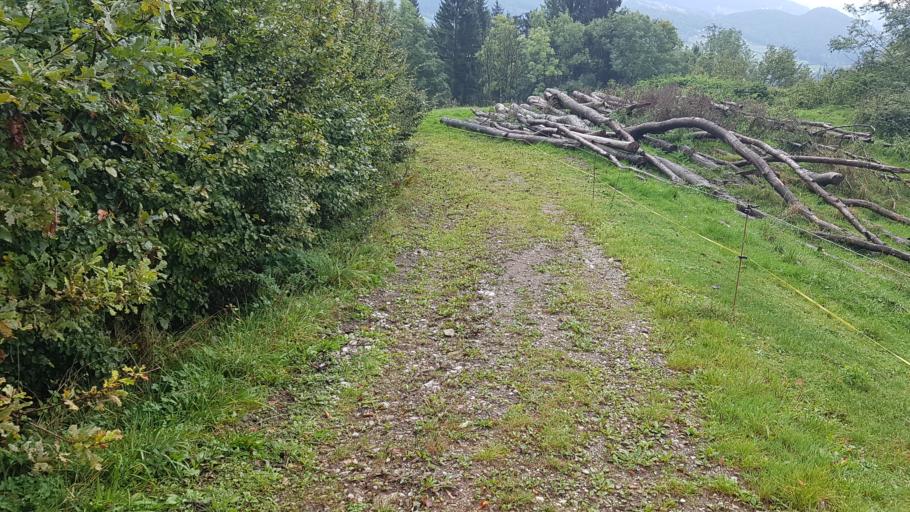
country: AT
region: Salzburg
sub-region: Politischer Bezirk Hallein
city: Puch bei Hallein
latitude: 47.7327
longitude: 13.1193
